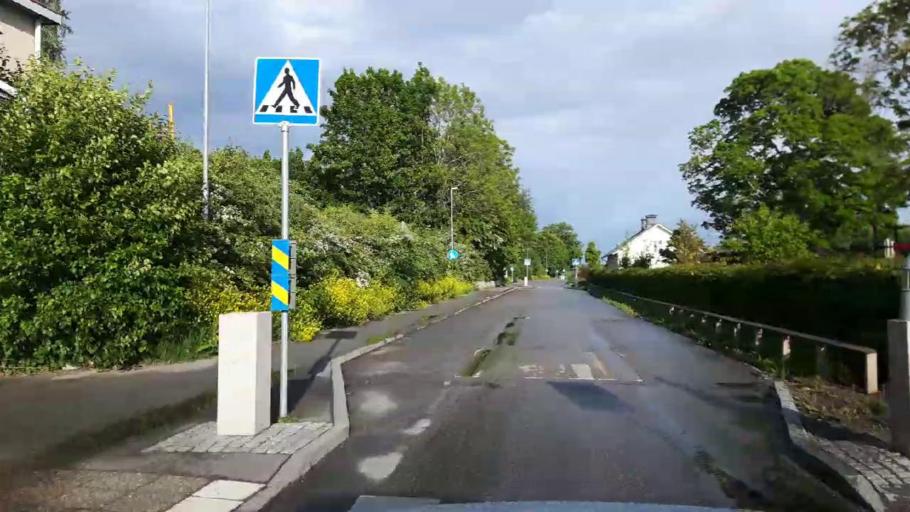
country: SE
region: Stockholm
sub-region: Upplands-Bro Kommun
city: Bro
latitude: 59.5107
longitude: 17.6394
